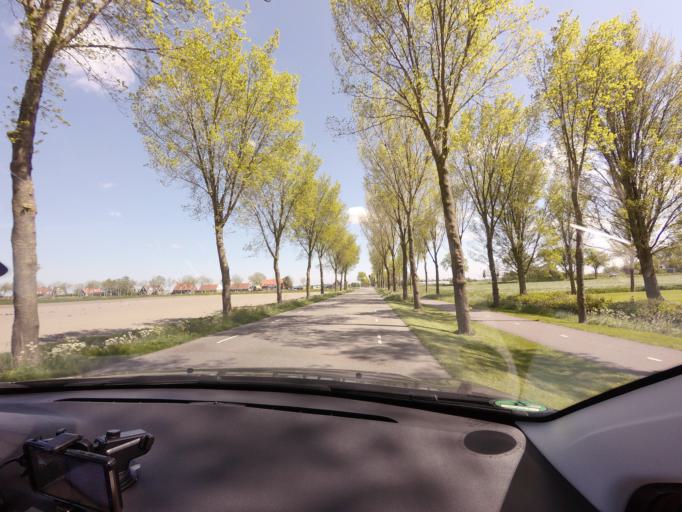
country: NL
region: North Holland
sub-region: Gemeente Beemster
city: Halfweg
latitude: 52.5546
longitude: 4.8849
